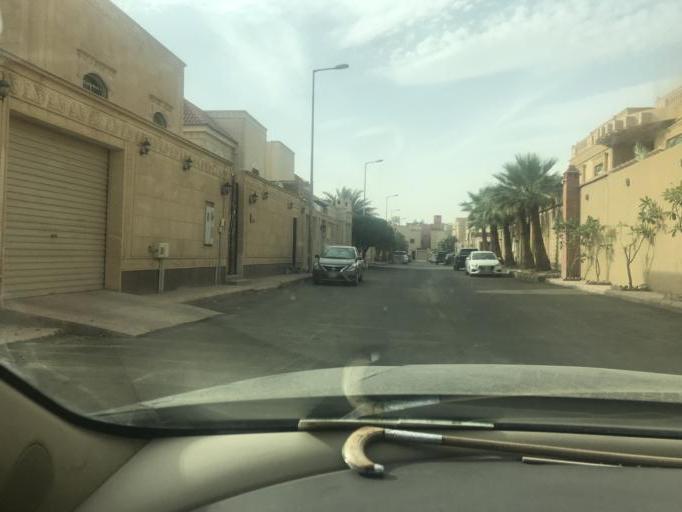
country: SA
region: Ar Riyad
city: Riyadh
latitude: 24.7989
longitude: 46.6698
